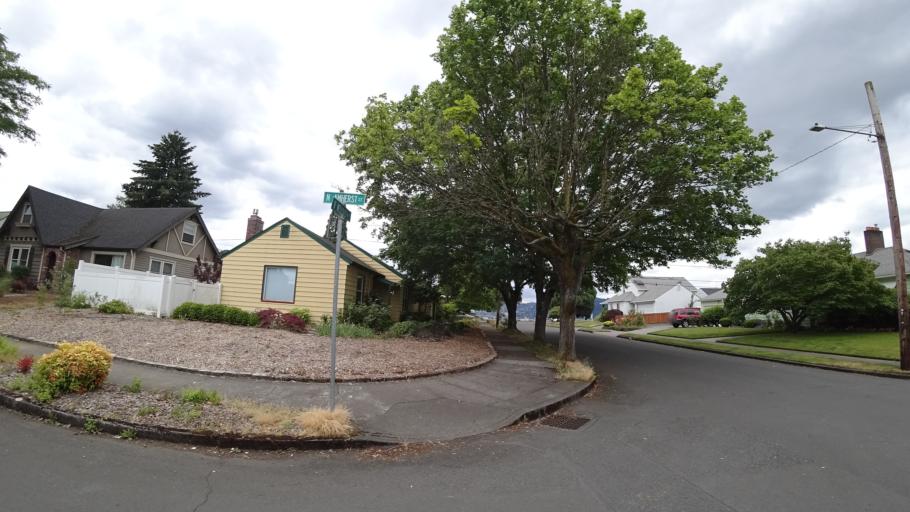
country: US
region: Oregon
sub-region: Multnomah County
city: Portland
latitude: 45.5758
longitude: -122.7160
